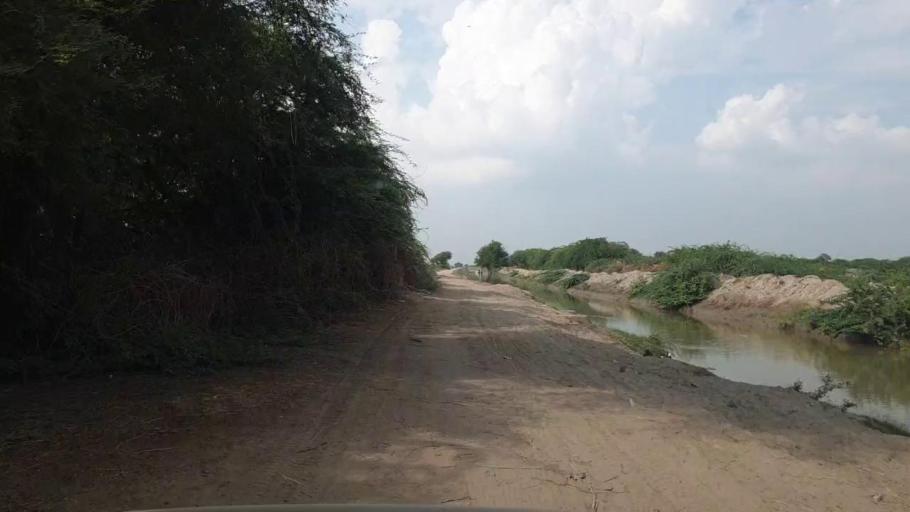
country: PK
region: Sindh
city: Badin
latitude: 24.5653
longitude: 68.6367
